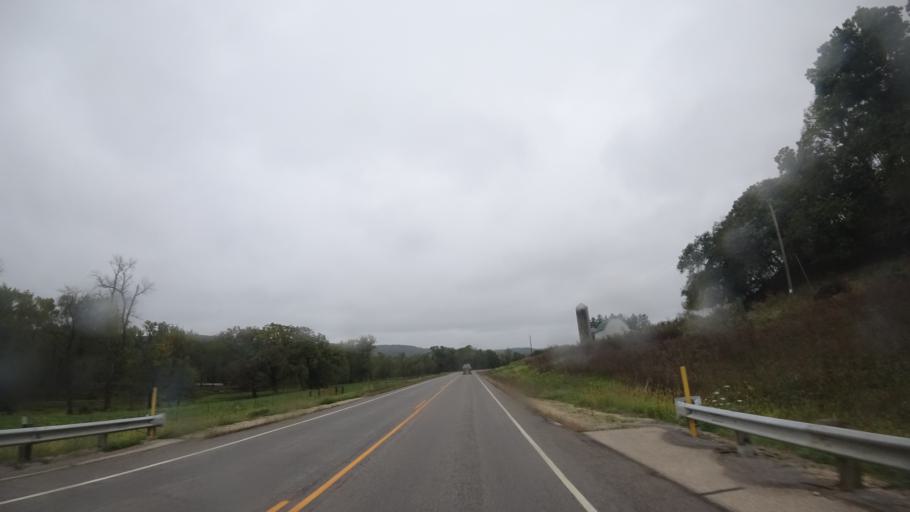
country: US
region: Wisconsin
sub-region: Crawford County
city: Prairie du Chien
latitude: 43.0365
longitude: -90.9884
